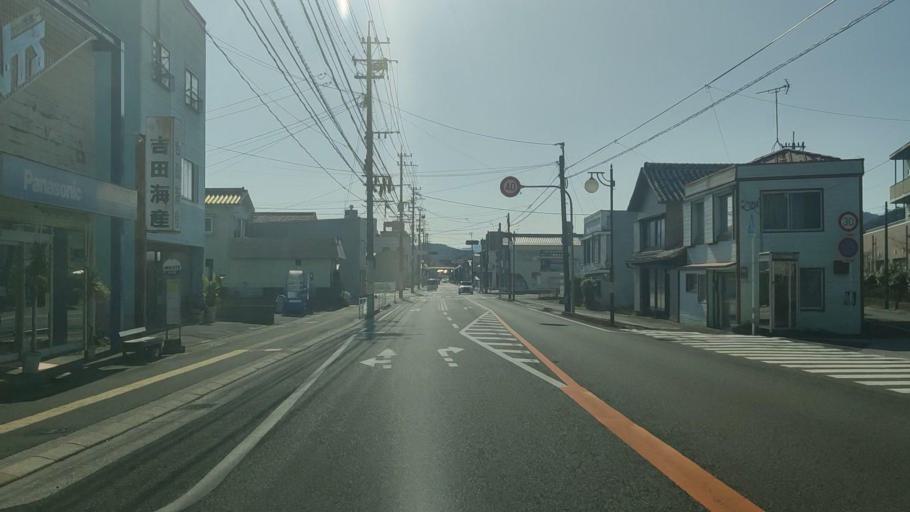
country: JP
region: Oita
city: Saiki
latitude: 32.9662
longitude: 131.9016
